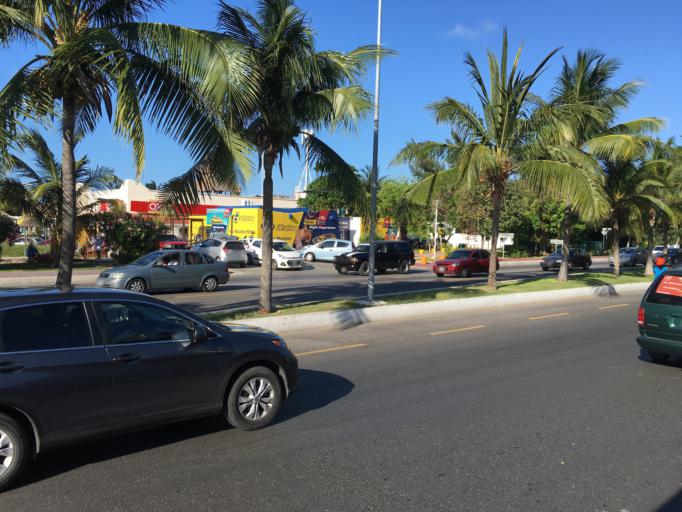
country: MX
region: Quintana Roo
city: Cancun
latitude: 21.1385
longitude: -86.7698
